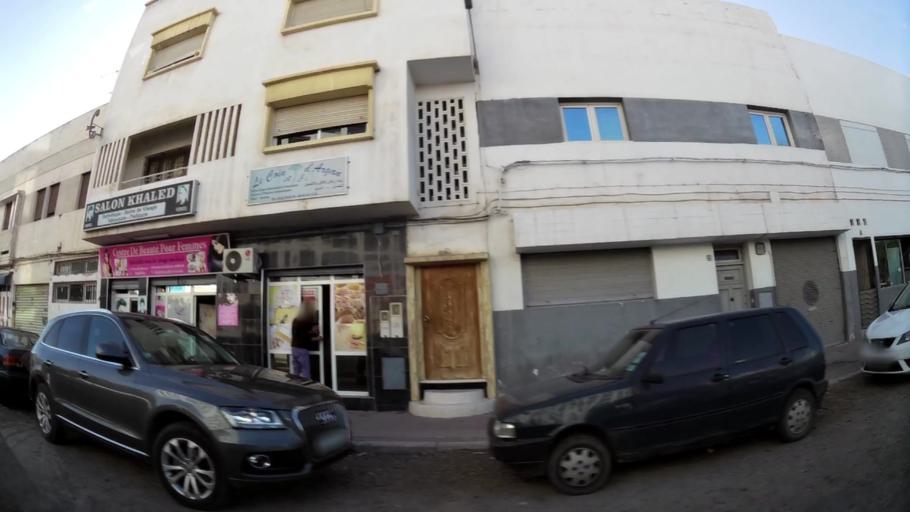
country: MA
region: Souss-Massa-Draa
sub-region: Agadir-Ida-ou-Tnan
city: Agadir
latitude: 30.4259
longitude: -9.5930
